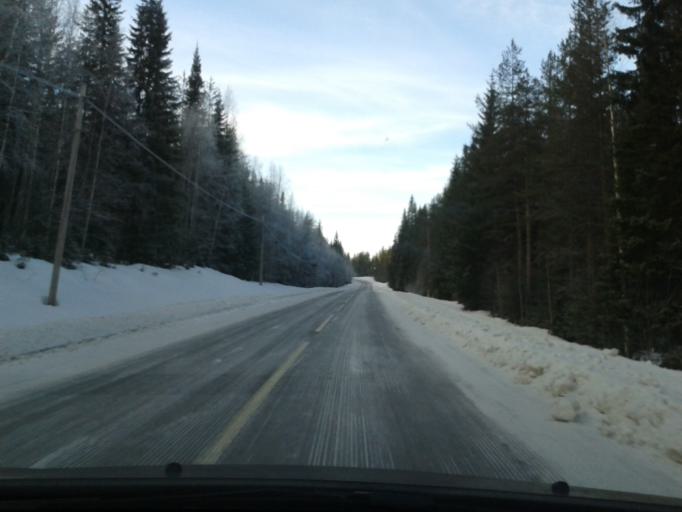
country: SE
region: Vaesternorrland
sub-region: OErnskoeldsviks Kommun
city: Bredbyn
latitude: 63.6595
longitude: 17.8566
